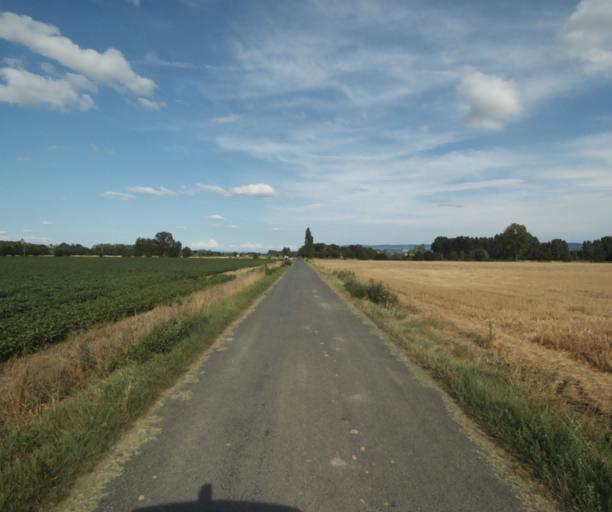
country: FR
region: Midi-Pyrenees
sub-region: Departement du Tarn
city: Puylaurens
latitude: 43.5200
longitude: 1.9919
